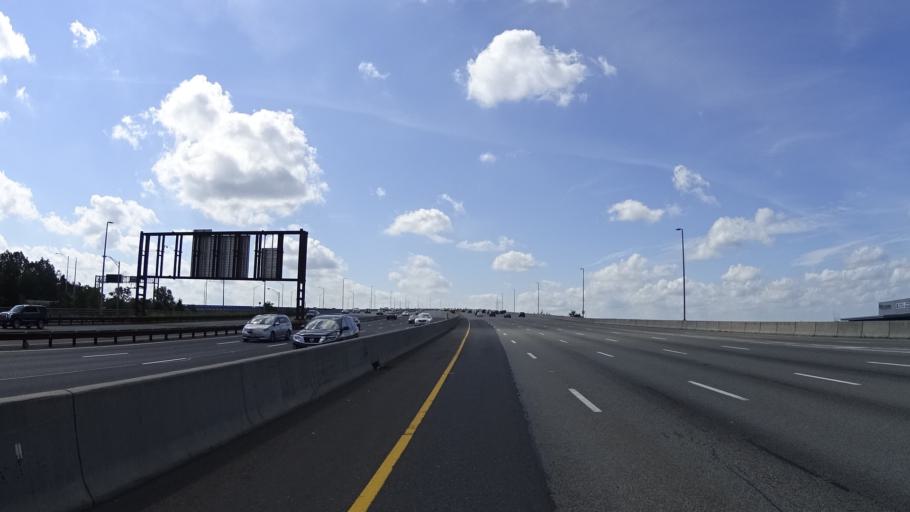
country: US
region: New Jersey
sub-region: Middlesex County
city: Fords
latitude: 40.5172
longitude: -74.3013
